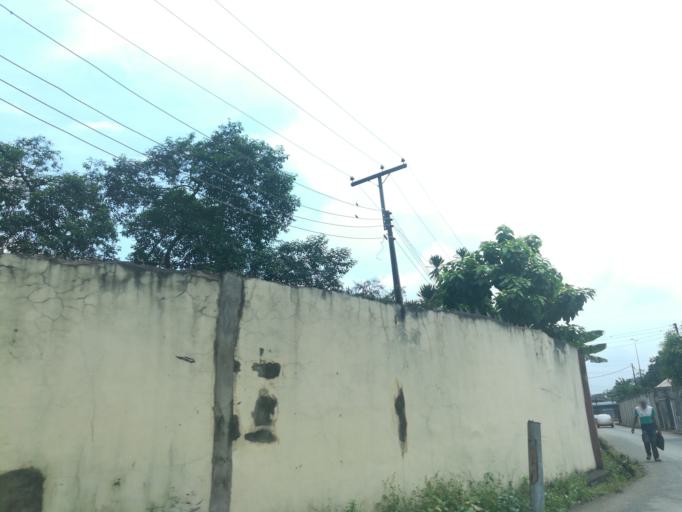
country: NG
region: Lagos
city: Ojota
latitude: 6.5662
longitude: 3.3655
